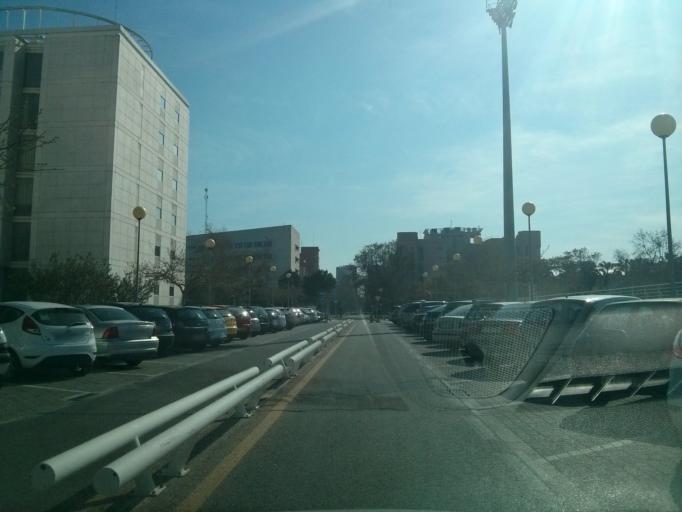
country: ES
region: Valencia
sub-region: Provincia de Valencia
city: Alboraya
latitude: 39.4814
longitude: -0.3389
